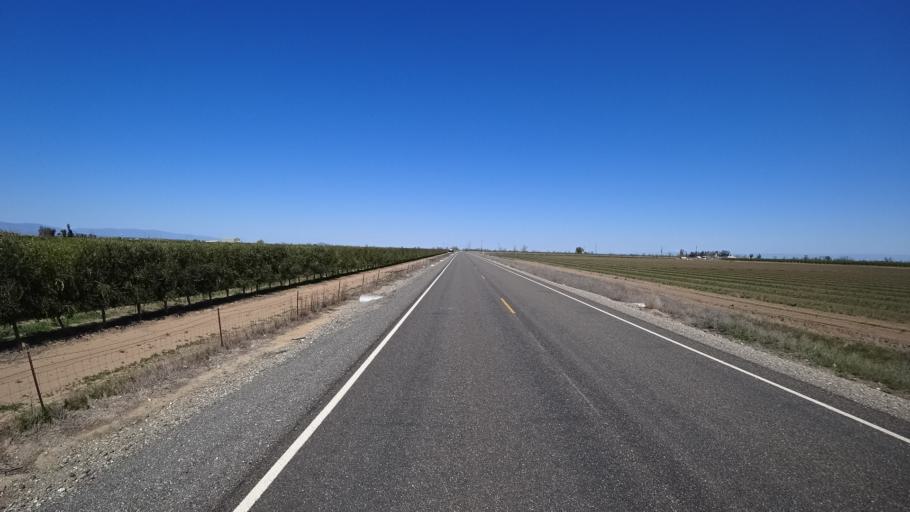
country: US
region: California
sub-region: Glenn County
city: Willows
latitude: 39.5937
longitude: -122.2500
